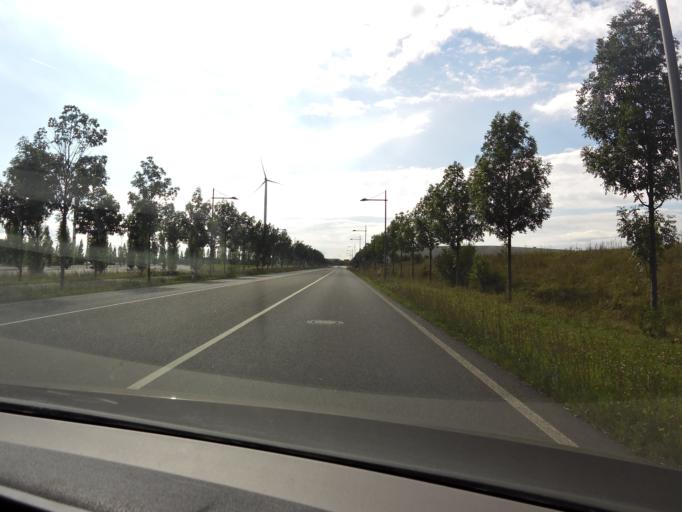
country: DE
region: Saxony
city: Taucha
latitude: 51.4120
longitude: 12.4457
